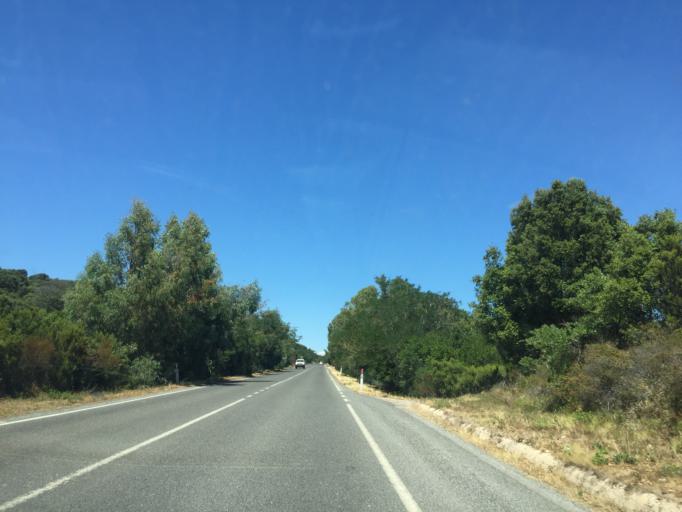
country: IT
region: Sardinia
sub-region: Provincia di Olbia-Tempio
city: Aglientu
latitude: 41.0783
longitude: 9.1161
